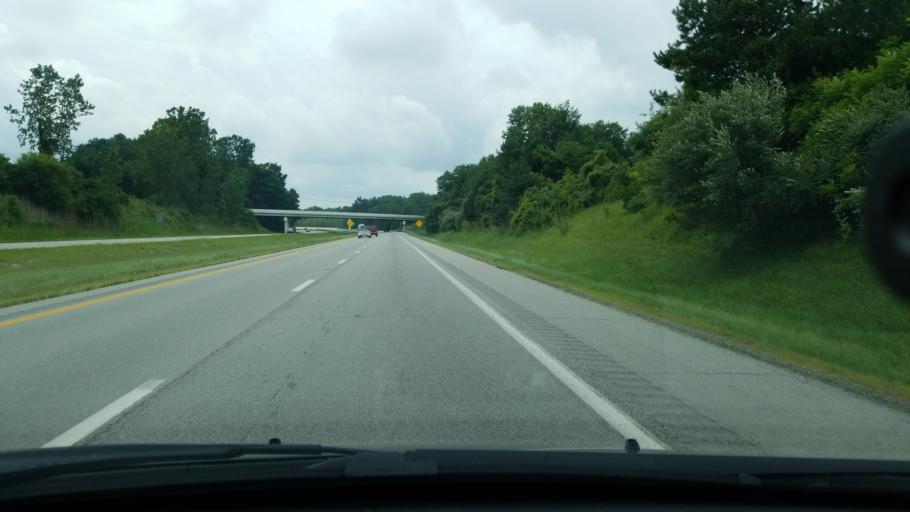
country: US
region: Ohio
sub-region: Erie County
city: Huron
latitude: 41.3798
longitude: -82.5739
